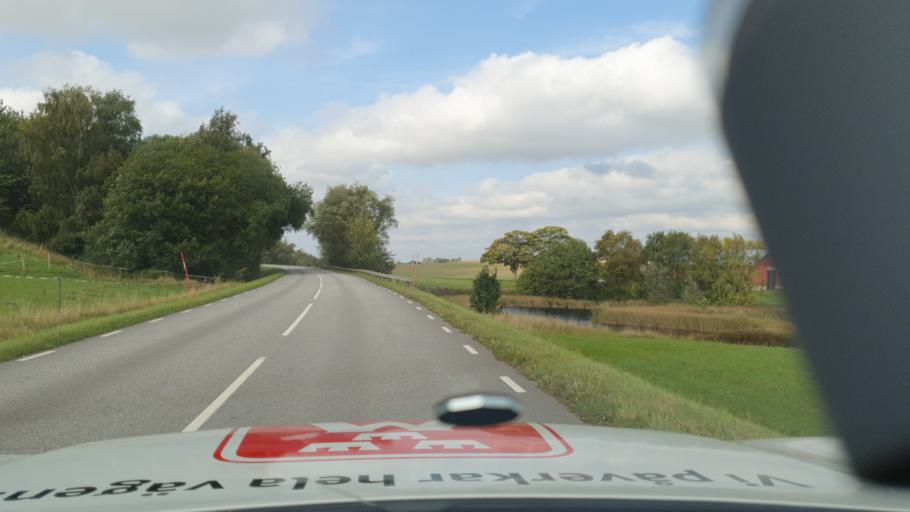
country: SE
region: Skane
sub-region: Malmo
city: Oxie
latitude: 55.4937
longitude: 13.1290
